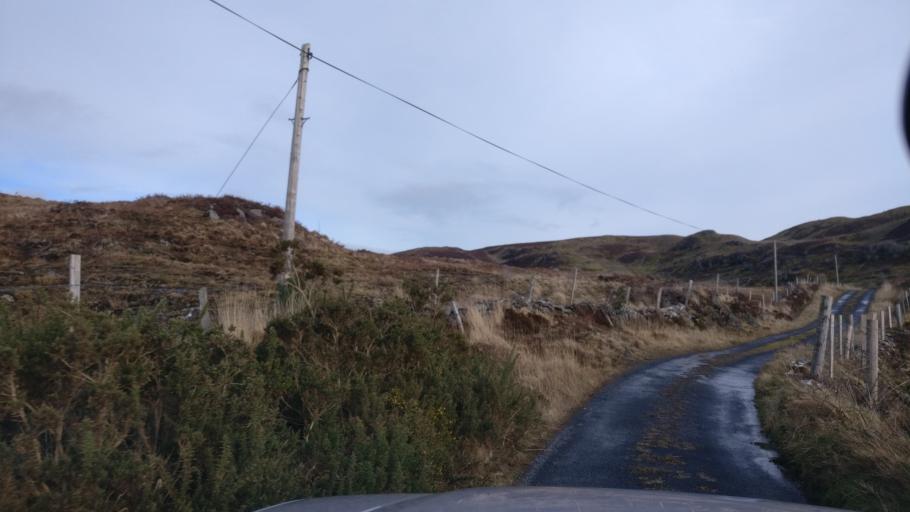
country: IE
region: Connaught
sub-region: County Galway
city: Oughterard
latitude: 53.5510
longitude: -9.4366
